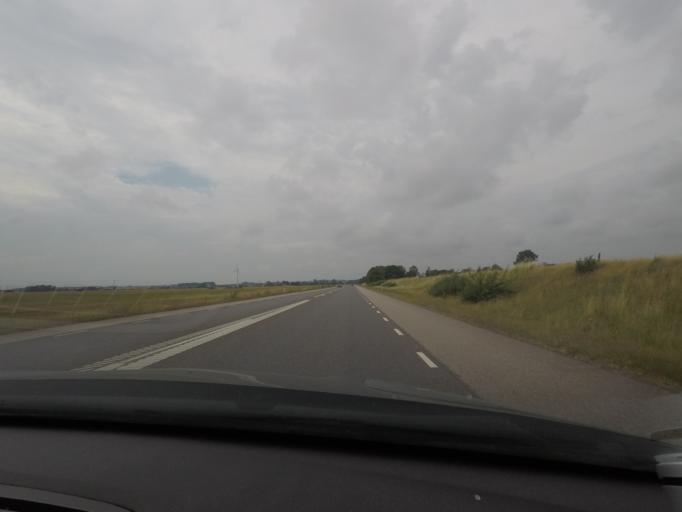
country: SE
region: Halland
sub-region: Laholms Kommun
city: Veinge
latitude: 56.5653
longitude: 13.0270
